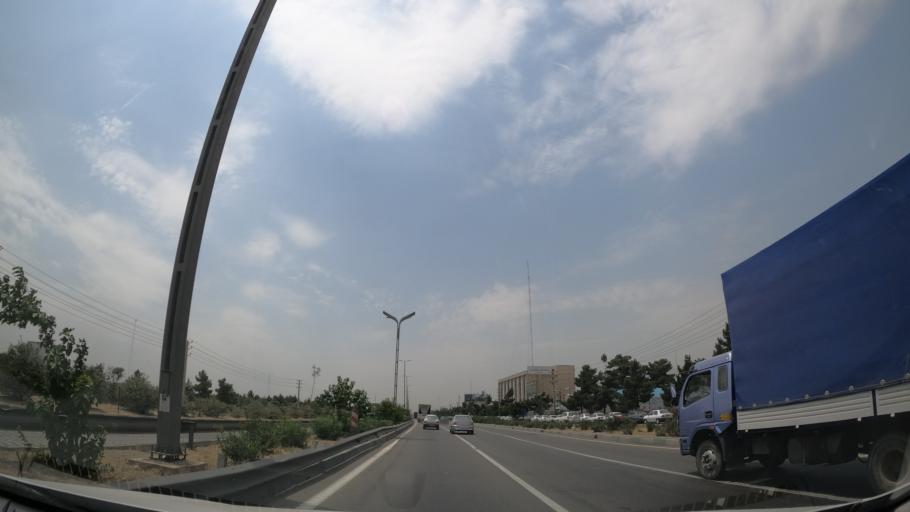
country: IR
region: Tehran
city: Shahr-e Qods
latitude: 35.7044
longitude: 51.1810
